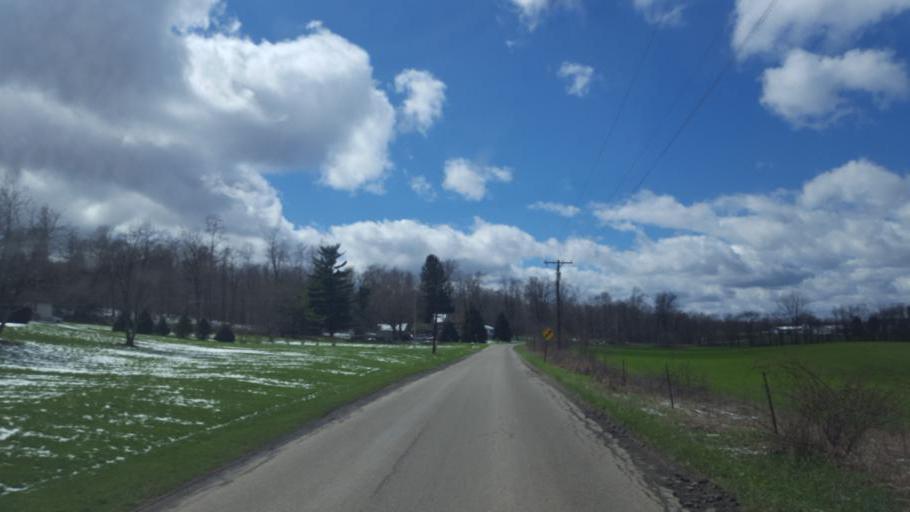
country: US
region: Ohio
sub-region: Knox County
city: Fredericktown
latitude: 40.5519
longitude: -82.6723
